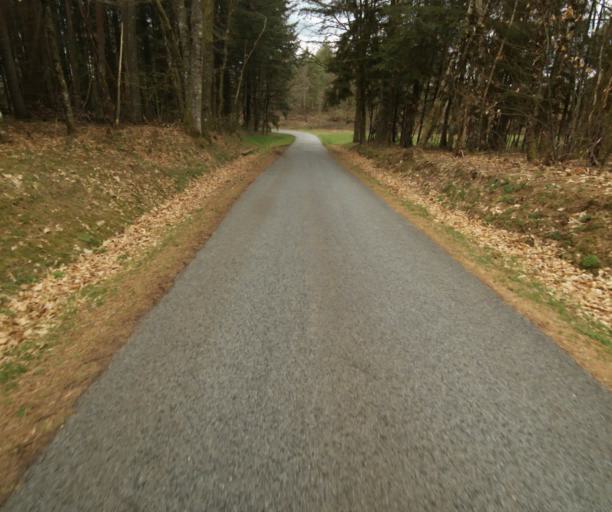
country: FR
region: Limousin
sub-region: Departement de la Correze
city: Correze
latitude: 45.3324
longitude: 1.9346
